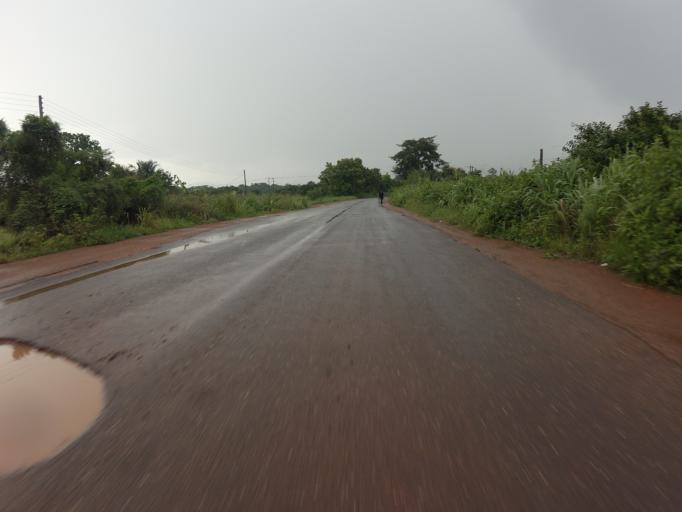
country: GH
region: Volta
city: Hohoe
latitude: 7.0549
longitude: 0.4275
